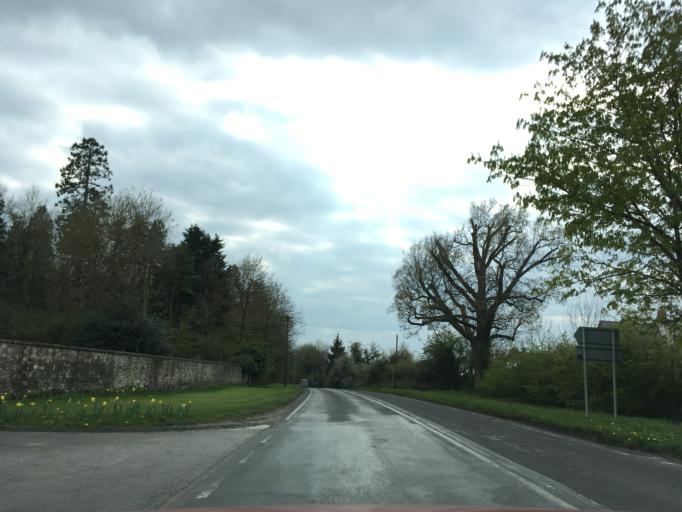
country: GB
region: England
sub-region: Oxfordshire
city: North Leigh
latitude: 51.8136
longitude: -1.4300
